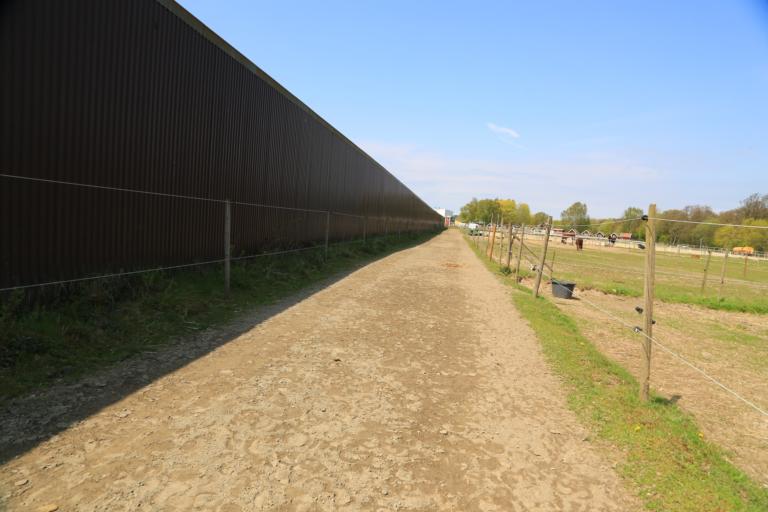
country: SE
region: Halland
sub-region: Varbergs Kommun
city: Varberg
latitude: 57.1275
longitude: 12.2956
